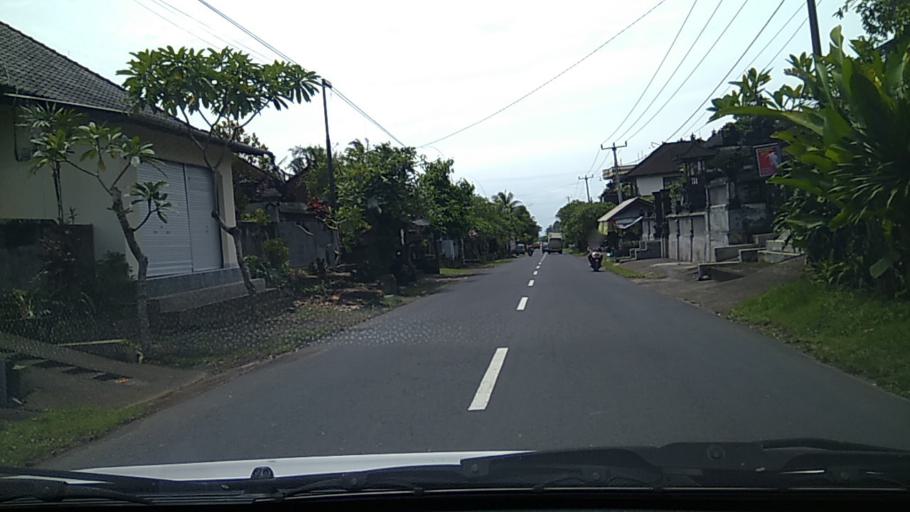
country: ID
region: Bali
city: Wanasari Baleran
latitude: -8.4725
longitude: 115.1368
